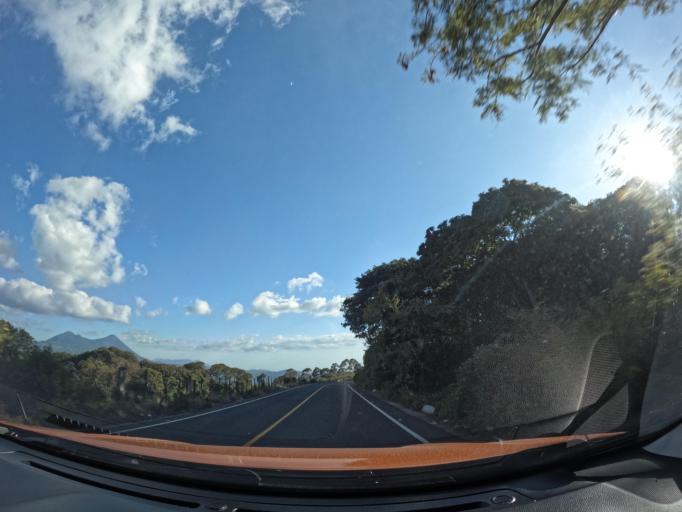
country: GT
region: Escuintla
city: Palin
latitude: 14.4637
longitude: -90.6940
